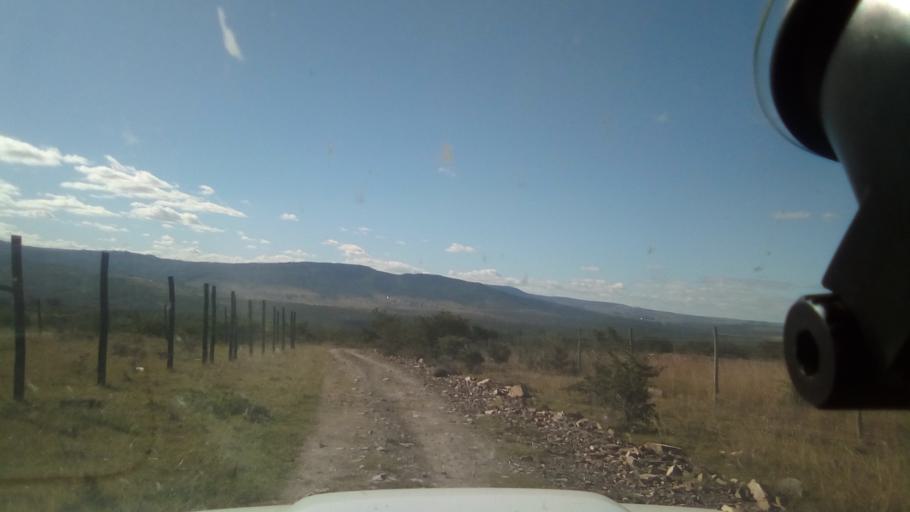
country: ZA
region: Eastern Cape
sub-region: Buffalo City Metropolitan Municipality
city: Bhisho
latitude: -32.7786
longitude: 27.3364
